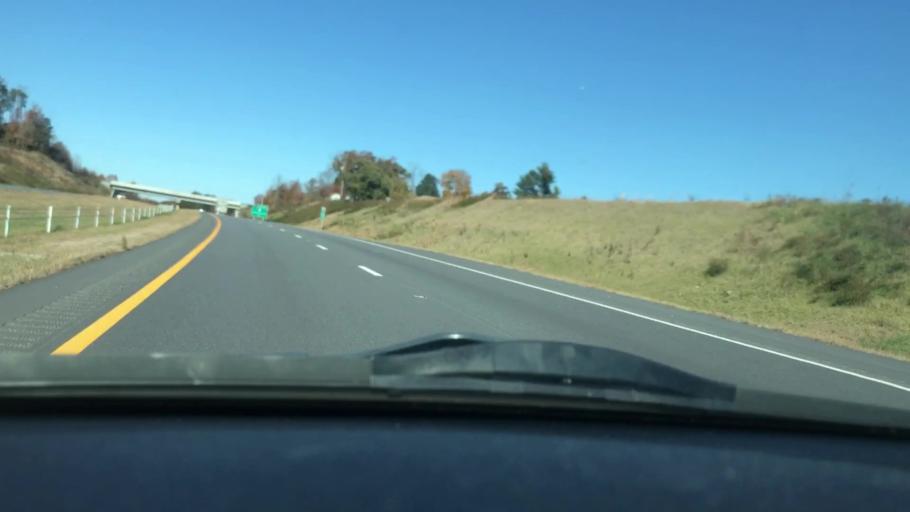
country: US
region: North Carolina
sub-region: Guilford County
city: Summerfield
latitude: 36.1811
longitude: -79.9320
